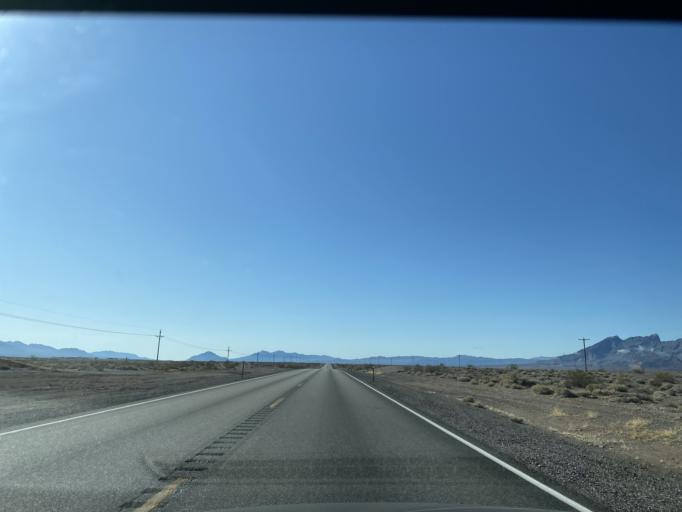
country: US
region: Nevada
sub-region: Nye County
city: Pahrump
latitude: 36.4563
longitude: -116.4218
